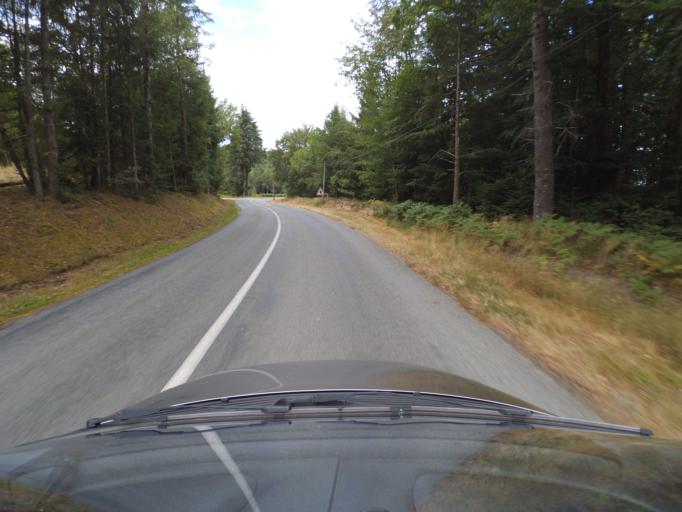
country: FR
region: Limousin
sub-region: Departement de la Haute-Vienne
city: Peyrat-le-Chateau
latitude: 45.8468
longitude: 1.9051
